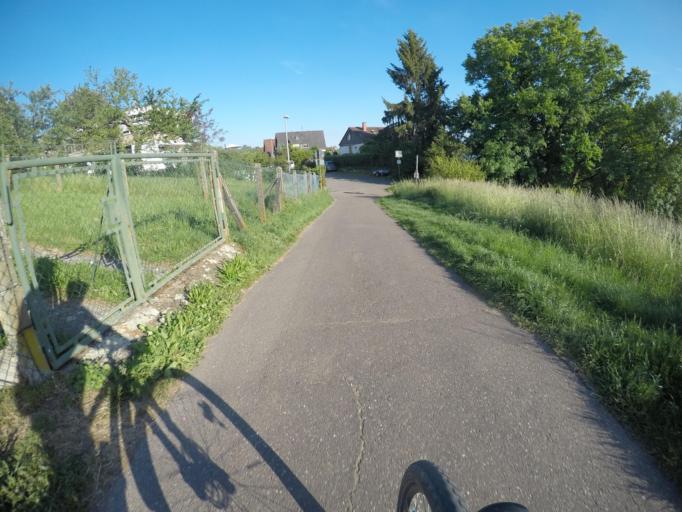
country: DE
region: Baden-Wuerttemberg
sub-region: Regierungsbezirk Stuttgart
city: Esslingen
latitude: 48.7570
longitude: 9.3256
